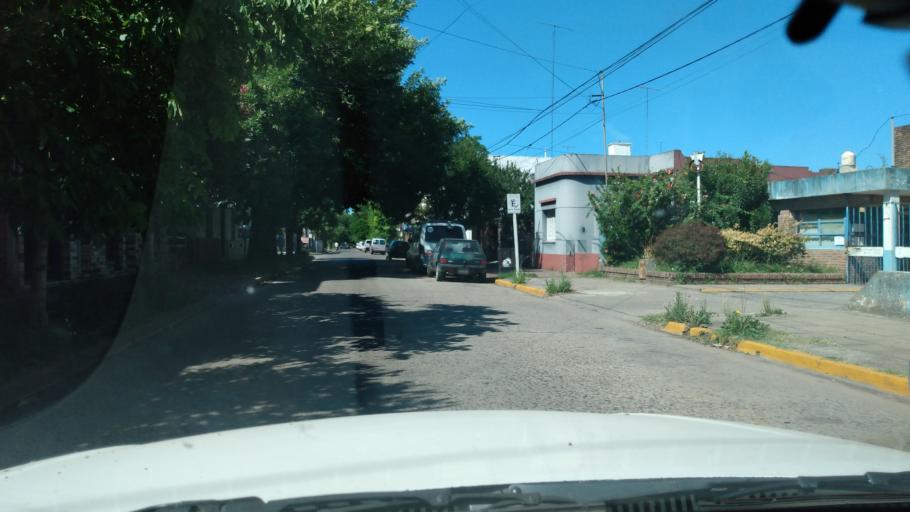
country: AR
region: Buenos Aires
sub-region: Partido de Lujan
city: Lujan
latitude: -34.5691
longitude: -59.1103
